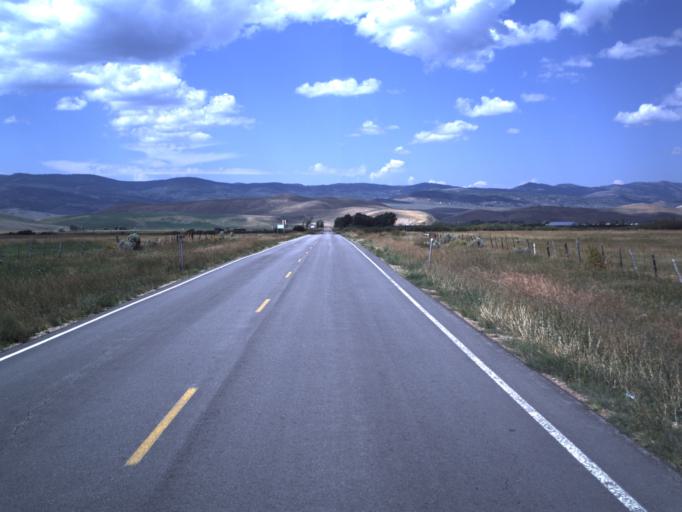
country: US
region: Utah
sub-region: Rich County
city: Randolph
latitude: 41.8335
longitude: -111.3270
